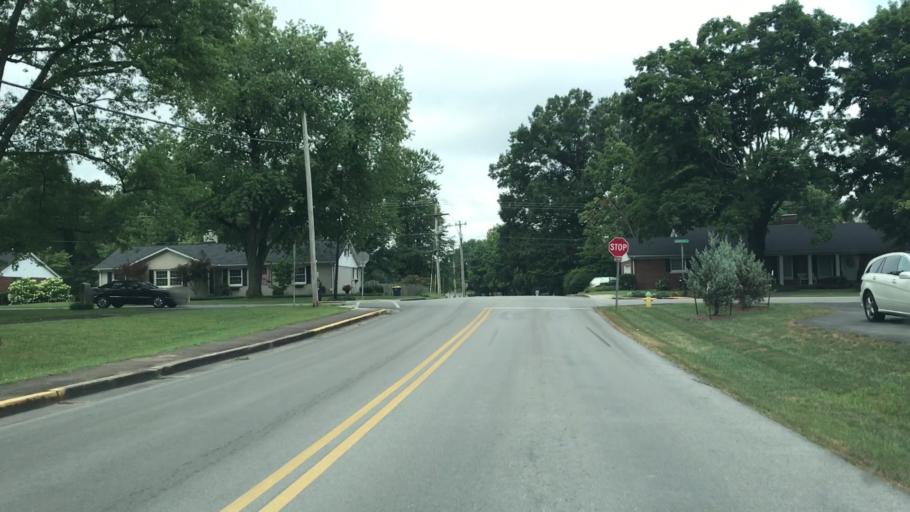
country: US
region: Kentucky
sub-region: Warren County
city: Bowling Green
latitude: 36.9859
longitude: -86.4160
